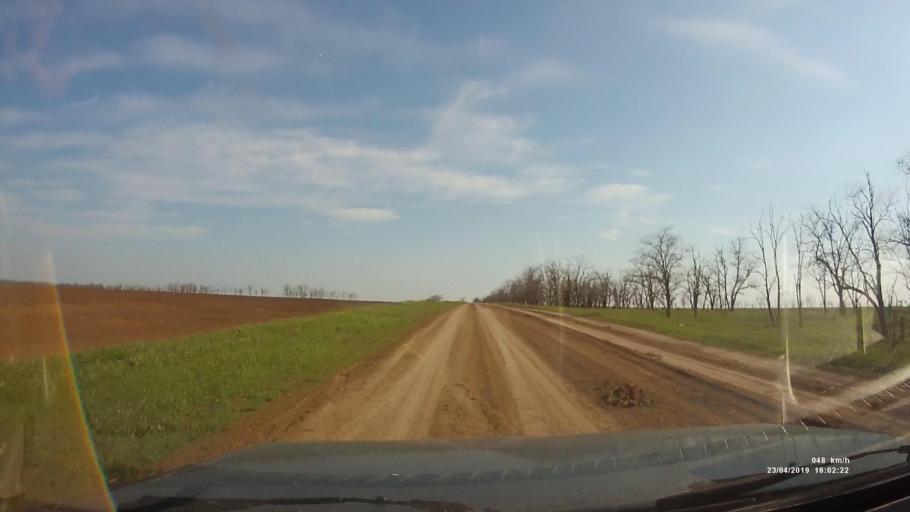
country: RU
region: Rostov
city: Remontnoye
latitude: 46.4949
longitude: 43.1070
